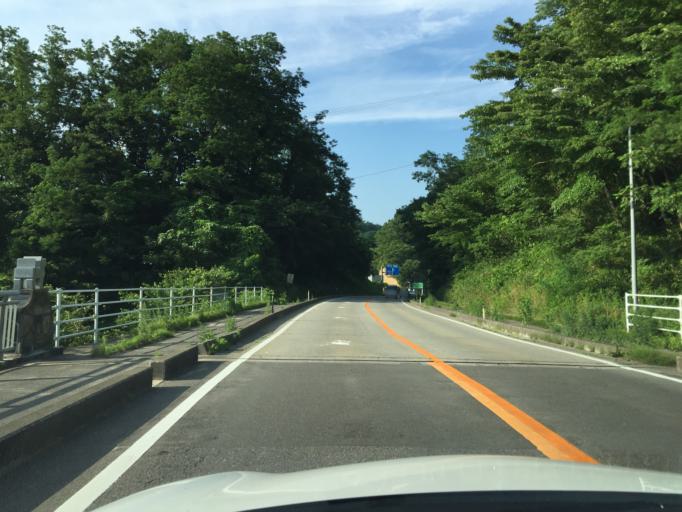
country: JP
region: Fukushima
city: Miharu
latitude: 37.4387
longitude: 140.5023
